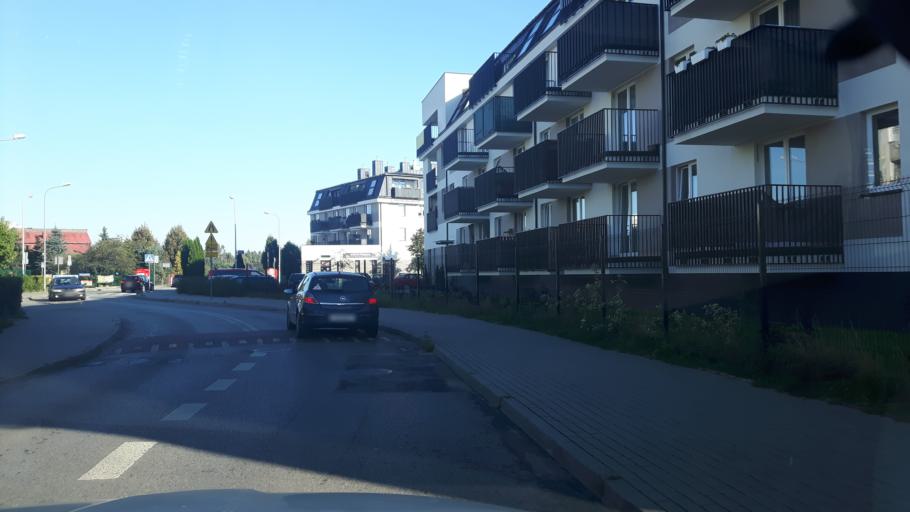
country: PL
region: Masovian Voivodeship
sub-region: Powiat legionowski
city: Stanislawow Pierwszy
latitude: 52.3604
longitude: 21.0395
